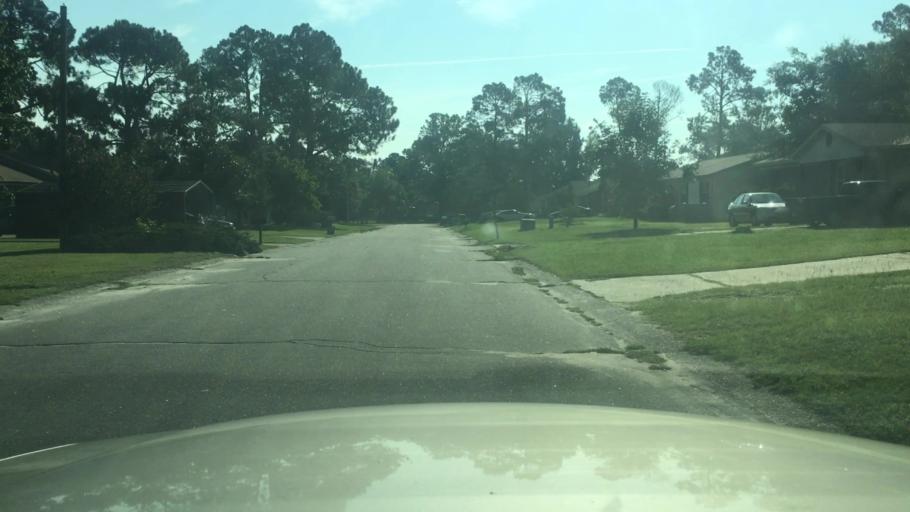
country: US
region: North Carolina
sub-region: Cumberland County
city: Spring Lake
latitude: 35.1585
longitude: -78.9103
